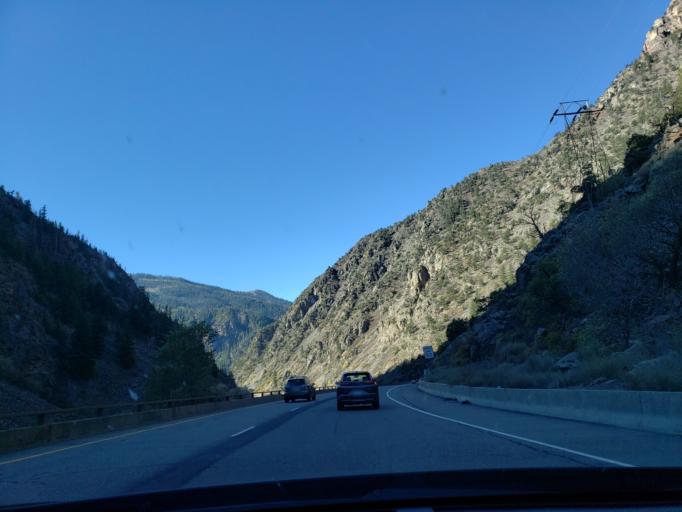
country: US
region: Colorado
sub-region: Garfield County
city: Glenwood Springs
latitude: 39.5675
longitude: -107.2305
